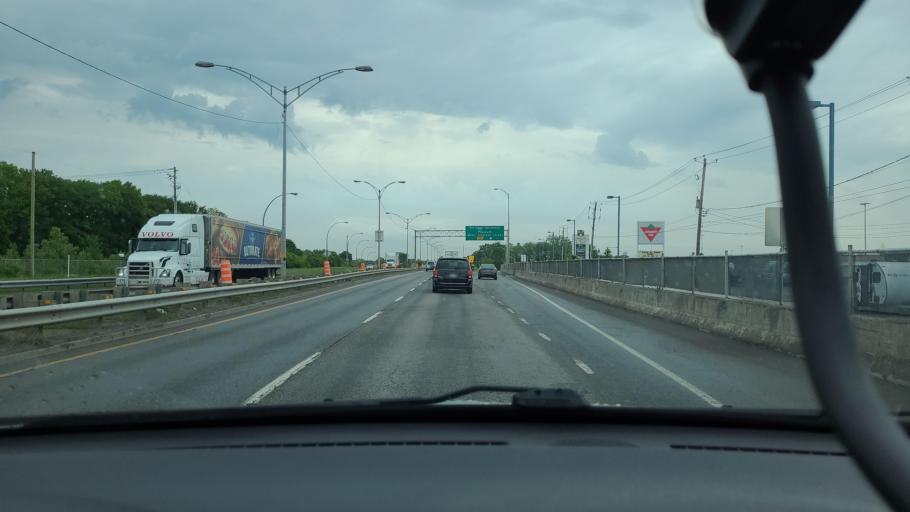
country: CA
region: Quebec
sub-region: Monteregie
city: Pincourt
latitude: 45.3862
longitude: -73.9982
